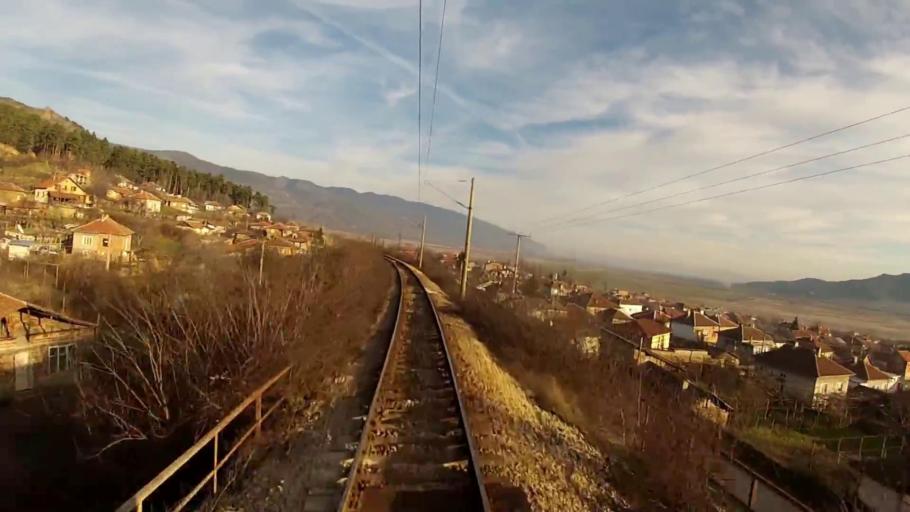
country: BG
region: Plovdiv
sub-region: Obshtina Karlovo
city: Klisura
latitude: 42.7158
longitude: 24.6009
